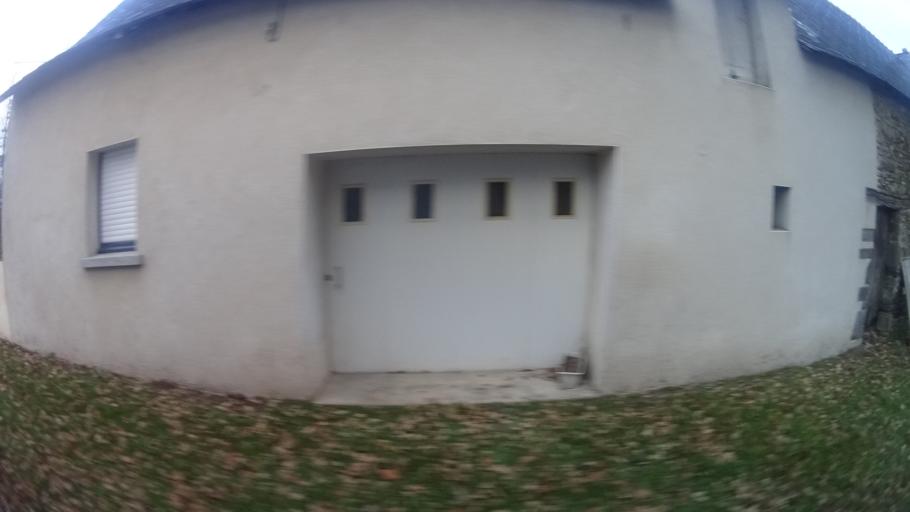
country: FR
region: Pays de la Loire
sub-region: Departement de la Loire-Atlantique
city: Avessac
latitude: 47.6434
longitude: -2.0248
